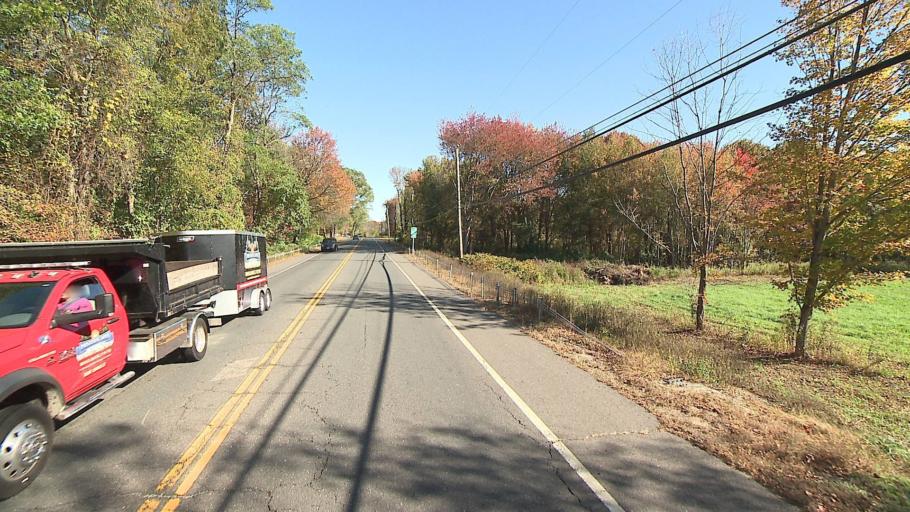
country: US
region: Connecticut
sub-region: Tolland County
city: Hebron
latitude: 41.6783
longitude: -72.3371
